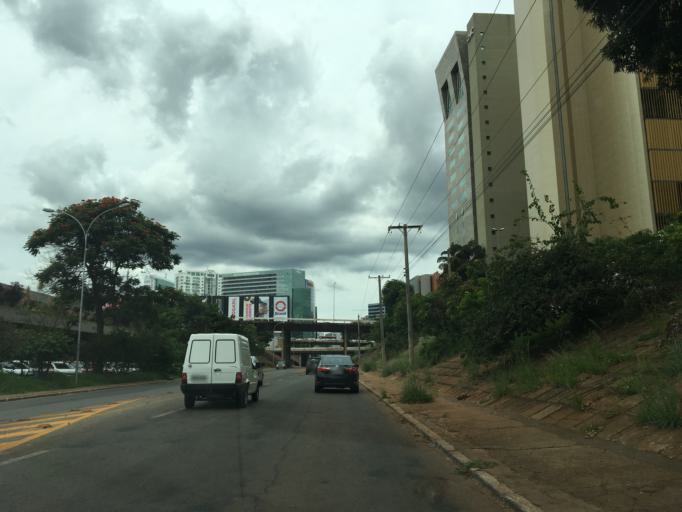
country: BR
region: Federal District
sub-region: Brasilia
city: Brasilia
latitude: -15.7914
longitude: -47.8796
